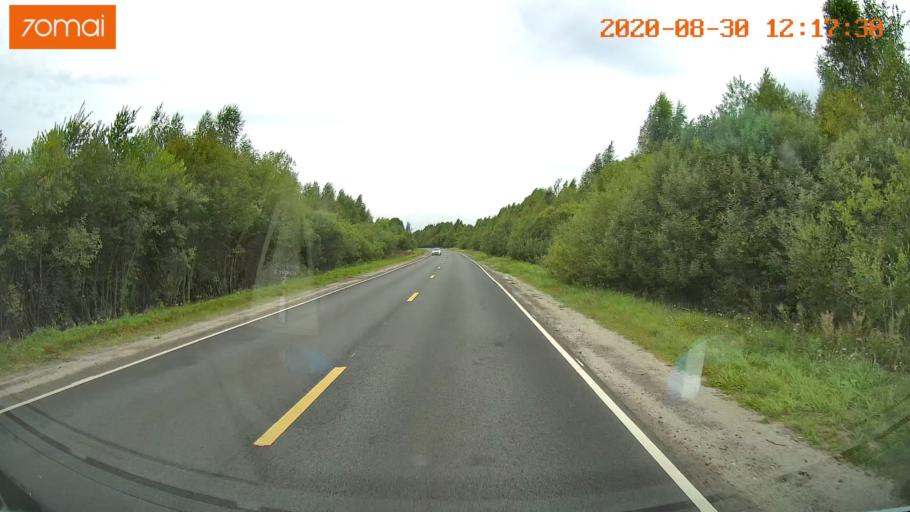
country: RU
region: Ivanovo
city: Yur'yevets
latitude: 57.3235
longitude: 42.9765
